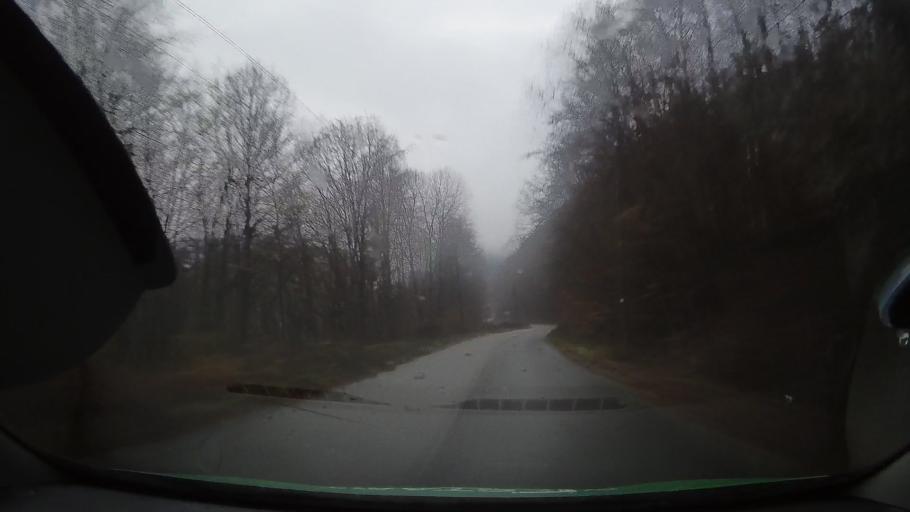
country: RO
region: Hunedoara
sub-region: Comuna Ribita
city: Ribita
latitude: 46.2488
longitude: 22.7471
